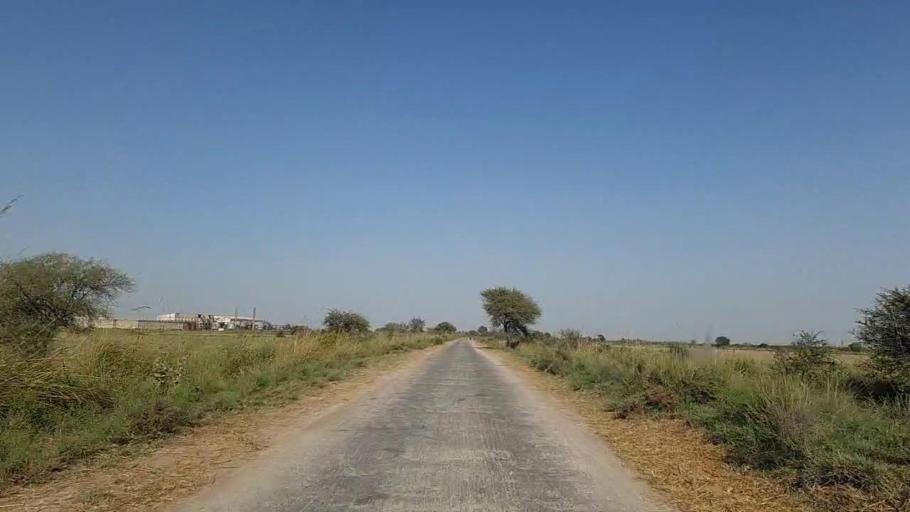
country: PK
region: Sindh
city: Chuhar Jamali
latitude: 24.5295
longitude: 68.1240
